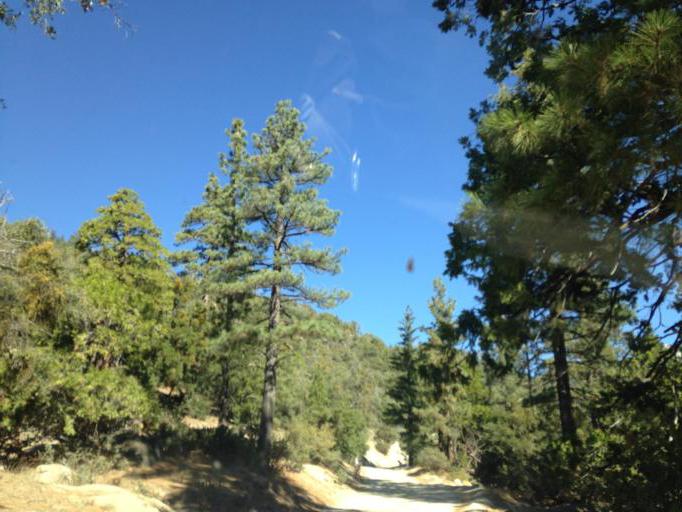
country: US
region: California
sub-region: Riverside County
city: Idyllwild-Pine Cove
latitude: 33.8104
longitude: -116.7491
